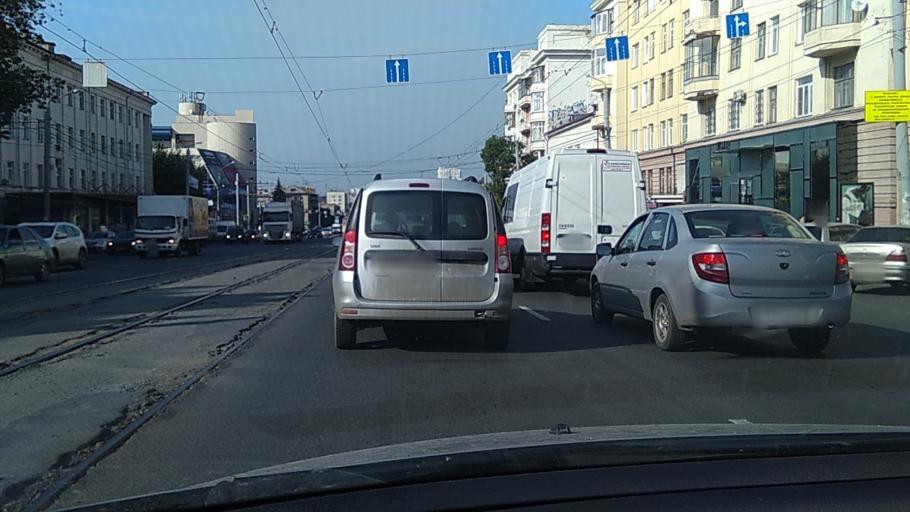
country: RU
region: Chelyabinsk
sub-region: Gorod Chelyabinsk
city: Chelyabinsk
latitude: 55.1585
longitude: 61.3892
